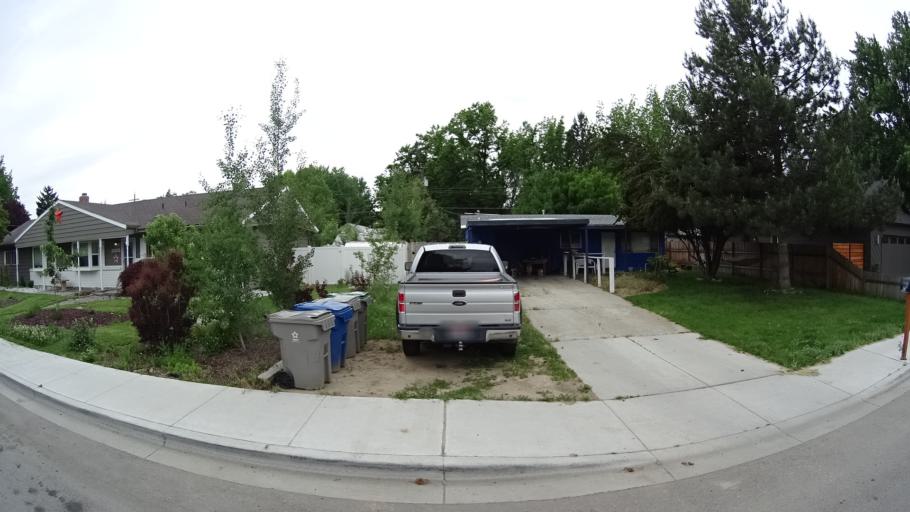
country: US
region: Idaho
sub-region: Ada County
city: Boise
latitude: 43.5826
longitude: -116.2067
